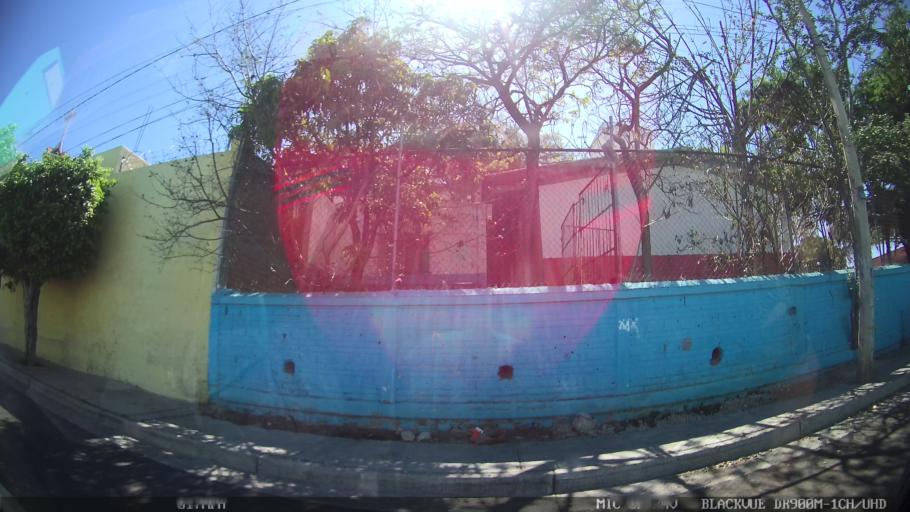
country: MX
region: Jalisco
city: Tlaquepaque
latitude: 20.6929
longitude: -103.2807
